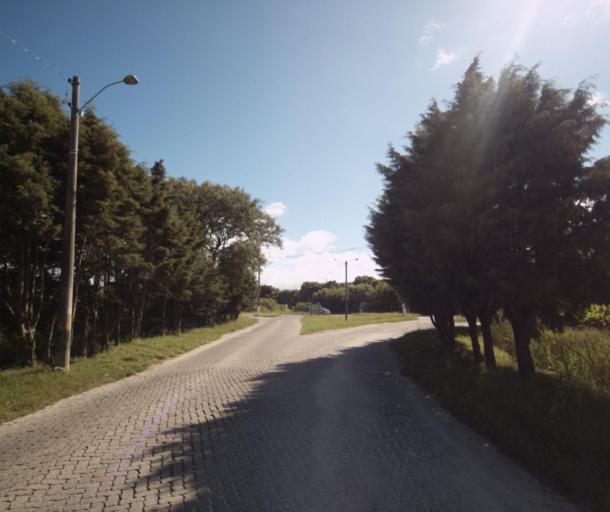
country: BR
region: Rio Grande do Sul
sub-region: Pelotas
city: Pelotas
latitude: -31.7536
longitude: -52.3592
